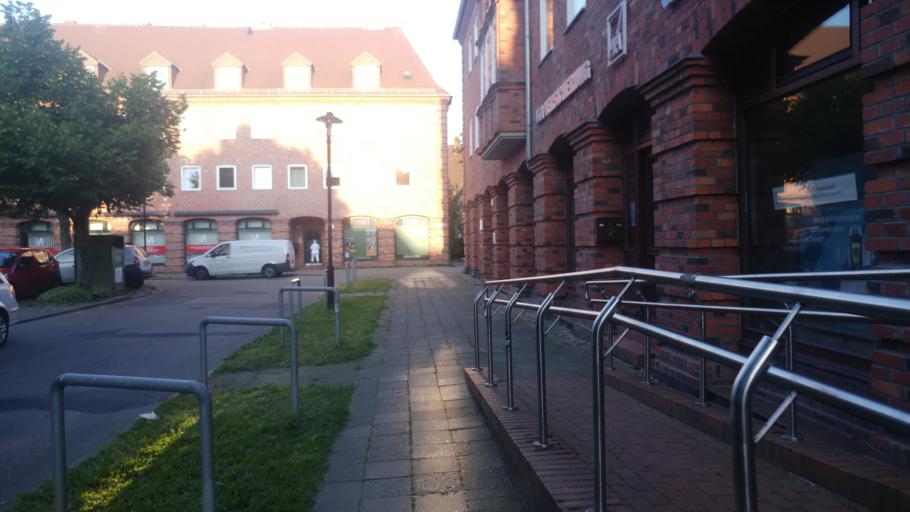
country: DE
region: Mecklenburg-Vorpommern
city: Kritzmow
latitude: 54.0976
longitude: 12.0827
